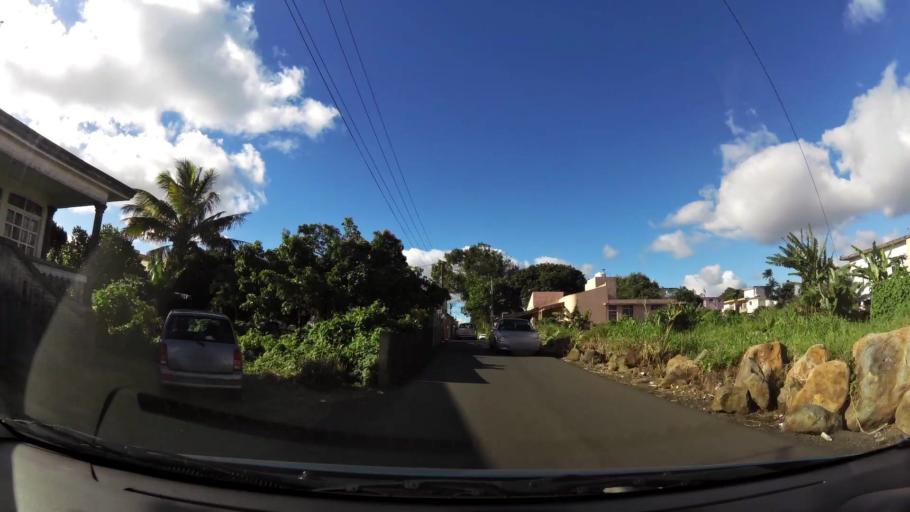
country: MU
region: Plaines Wilhems
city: Curepipe
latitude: -20.2893
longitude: 57.5170
